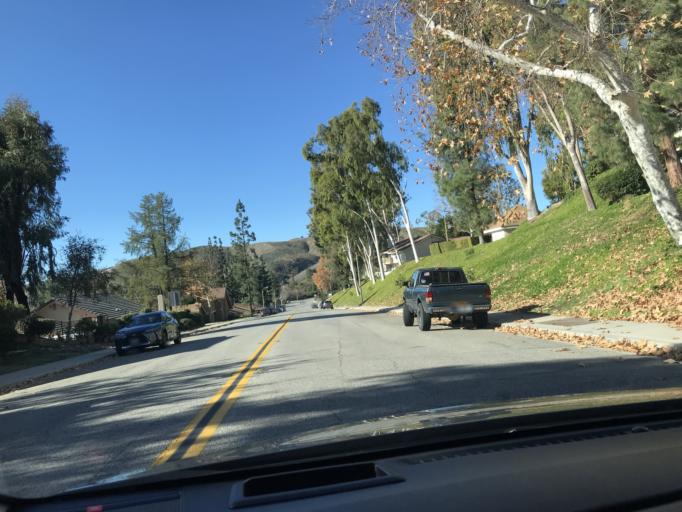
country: US
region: California
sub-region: Ventura County
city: Oak Park
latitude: 34.1771
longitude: -118.7570
